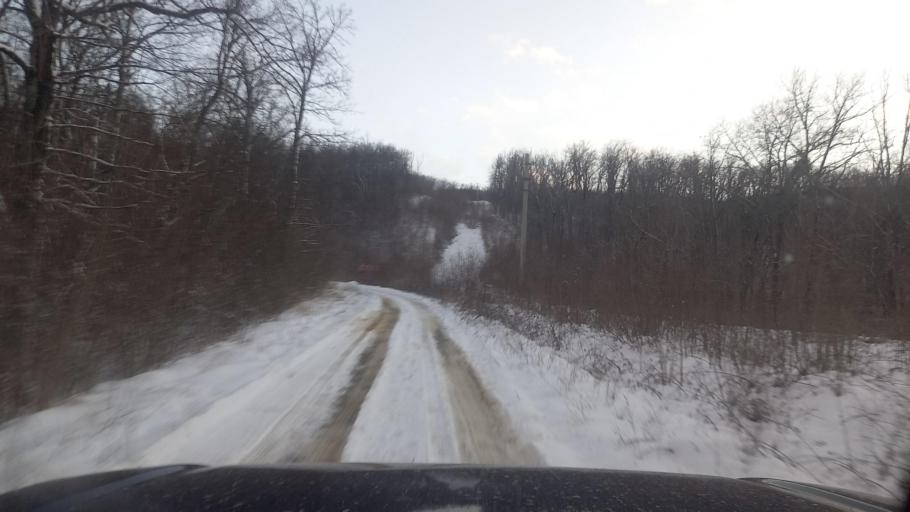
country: RU
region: Krasnodarskiy
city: Smolenskaya
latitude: 44.6697
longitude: 38.7961
